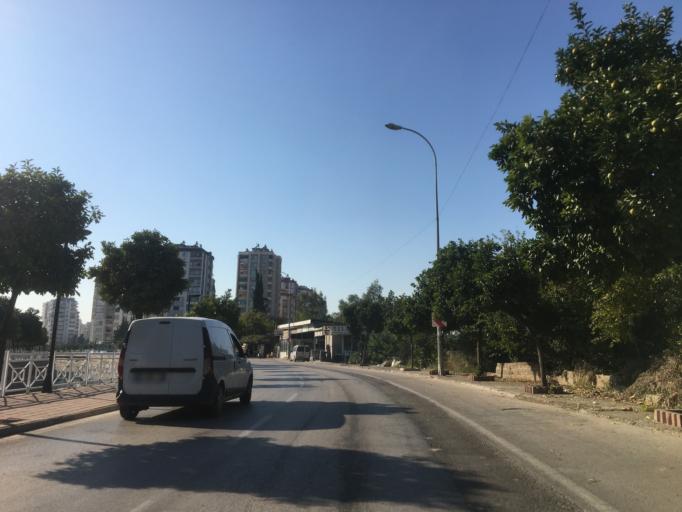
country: TR
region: Adana
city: Seyhan
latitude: 37.0303
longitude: 35.2809
